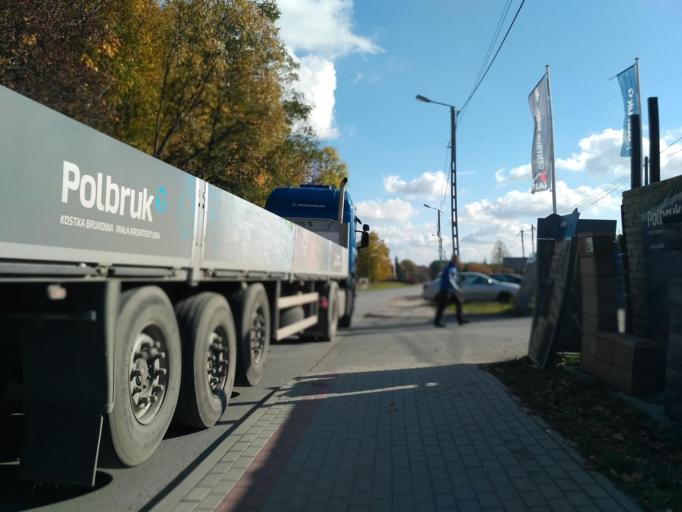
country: PL
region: Subcarpathian Voivodeship
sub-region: Powiat rzeszowski
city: Glogow Malopolski
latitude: 50.1521
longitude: 21.9456
